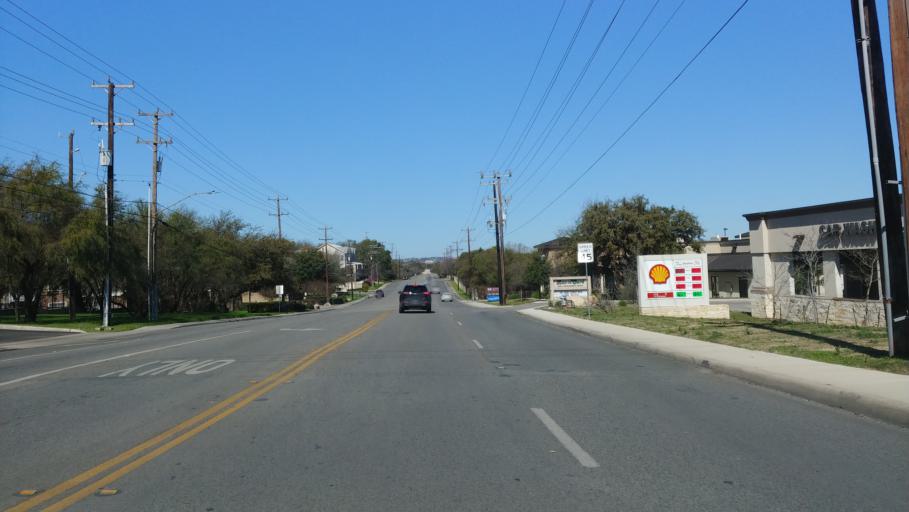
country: US
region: Texas
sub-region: Bexar County
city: Shavano Park
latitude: 29.5646
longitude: -98.5582
